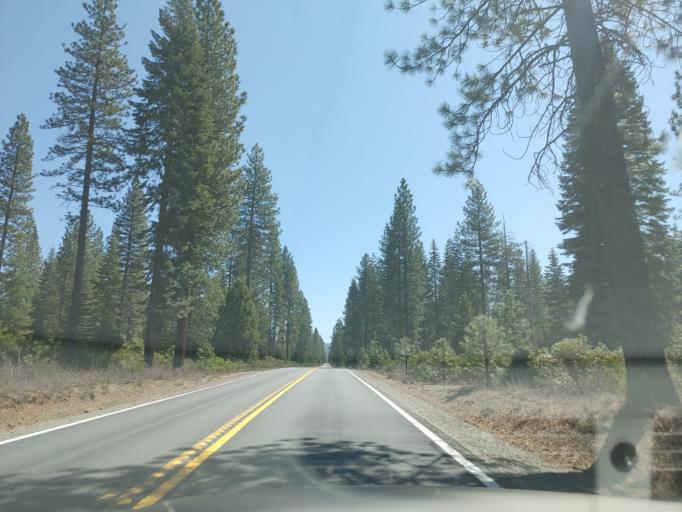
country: US
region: California
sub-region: Siskiyou County
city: McCloud
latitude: 41.2614
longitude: -121.8450
